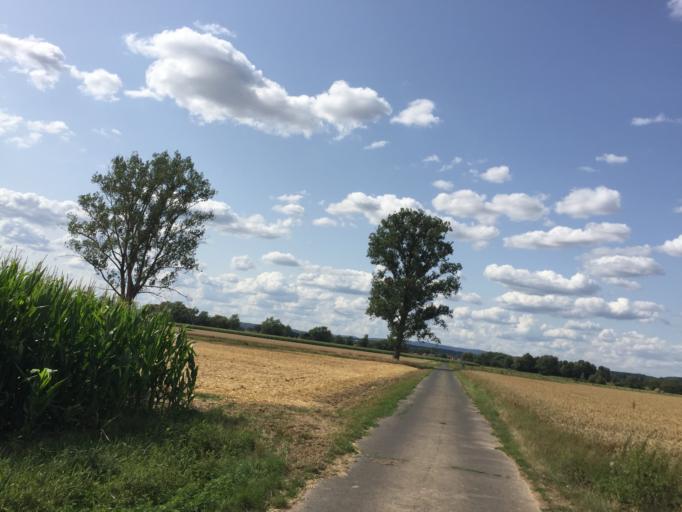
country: DE
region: Hesse
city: Schwalmstadt
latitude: 50.9006
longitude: 9.2568
